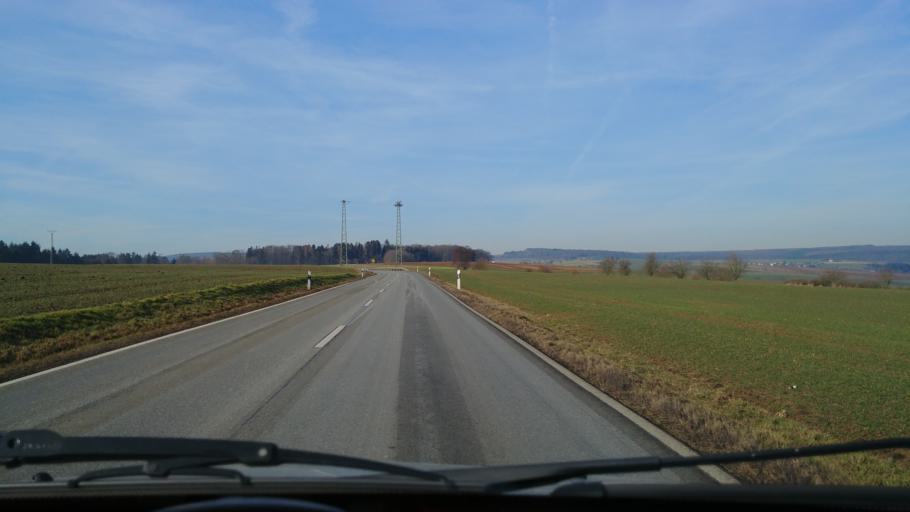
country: DE
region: Rheinland-Pfalz
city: Ehr
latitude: 50.2441
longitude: 7.7919
